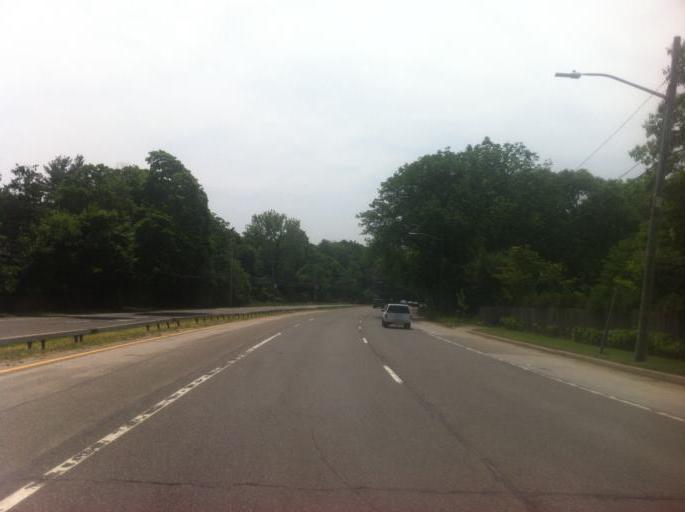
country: US
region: New York
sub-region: Nassau County
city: Glen Head
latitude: 40.8481
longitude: -73.6165
